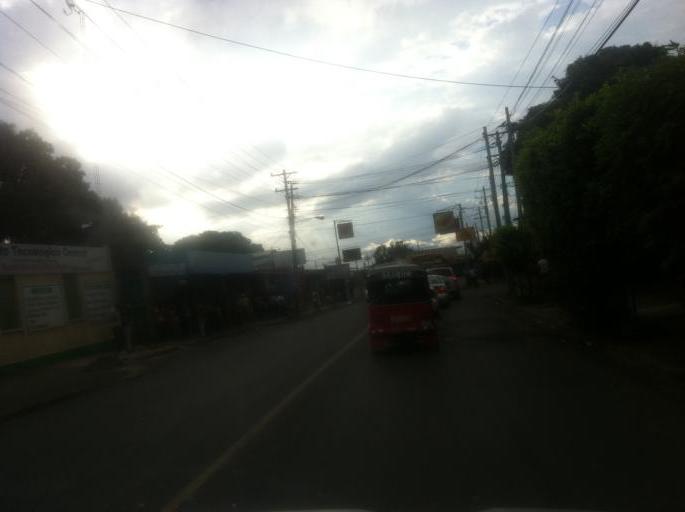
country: NI
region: Managua
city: Managua
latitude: 12.1216
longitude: -86.2426
